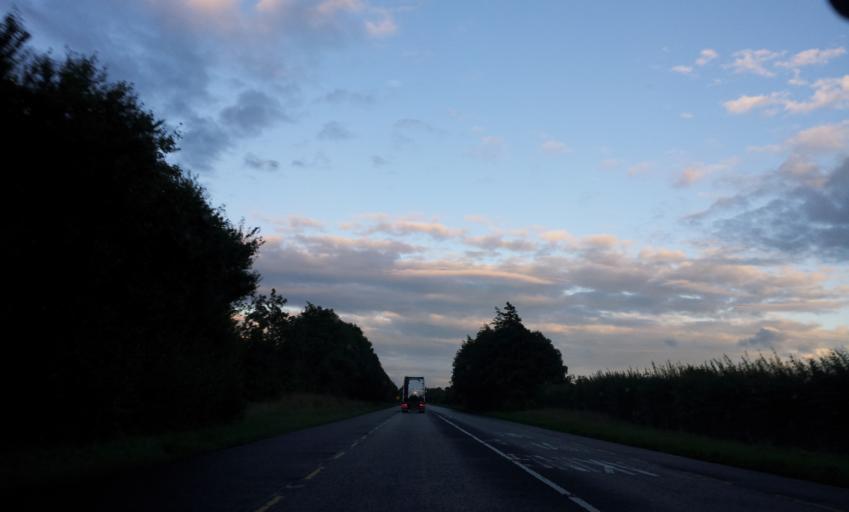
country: IE
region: Munster
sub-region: County Limerick
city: Rathkeale
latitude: 52.5305
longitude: -8.9107
